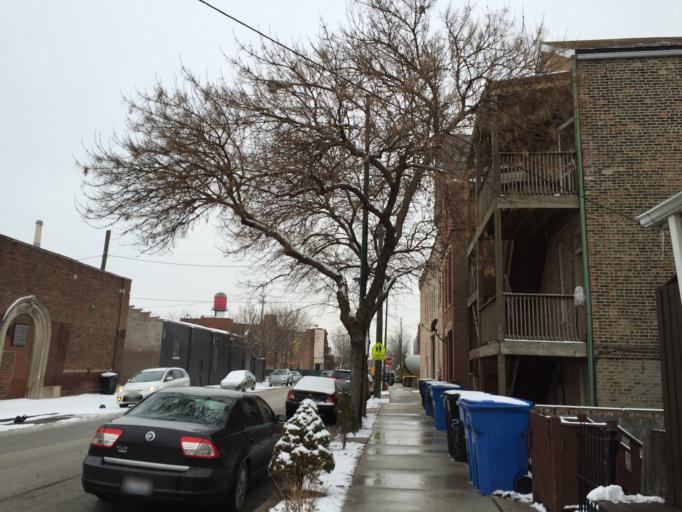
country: US
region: Illinois
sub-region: Cook County
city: Chicago
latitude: 41.8540
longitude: -87.6472
